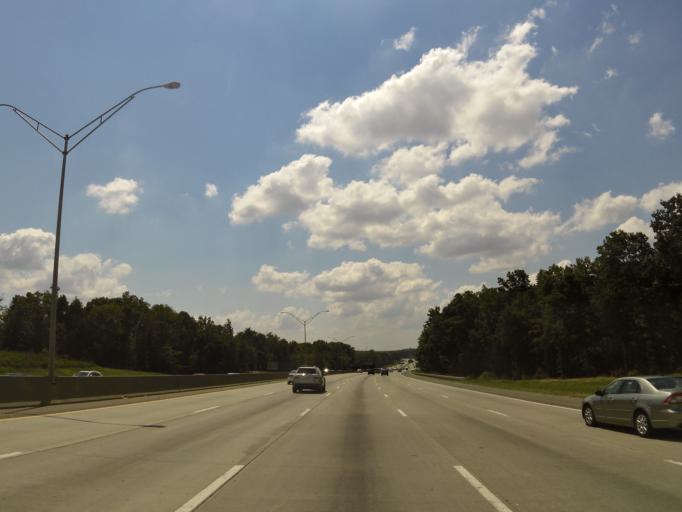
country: US
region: North Carolina
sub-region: Cabarrus County
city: Harrisburg
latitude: 35.3258
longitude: -80.7471
